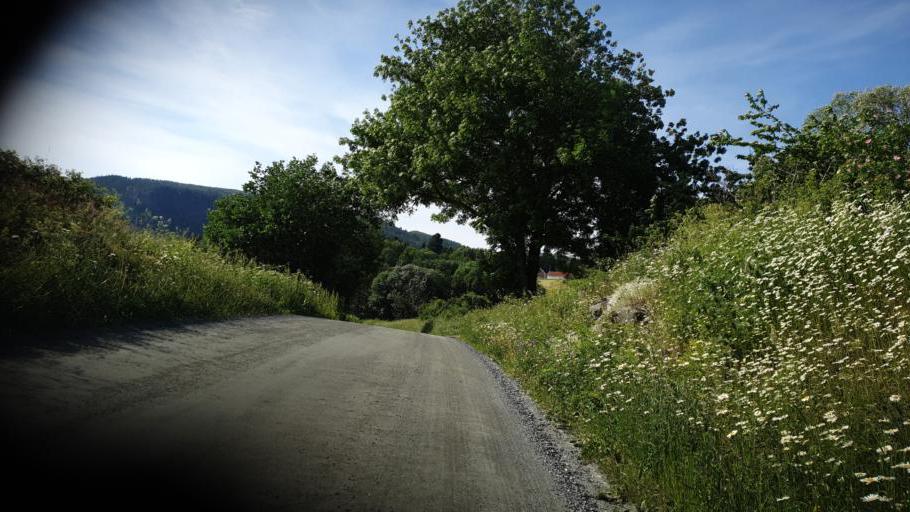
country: NO
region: Sor-Trondelag
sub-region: Trondheim
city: Trondheim
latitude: 63.5719
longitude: 10.4054
